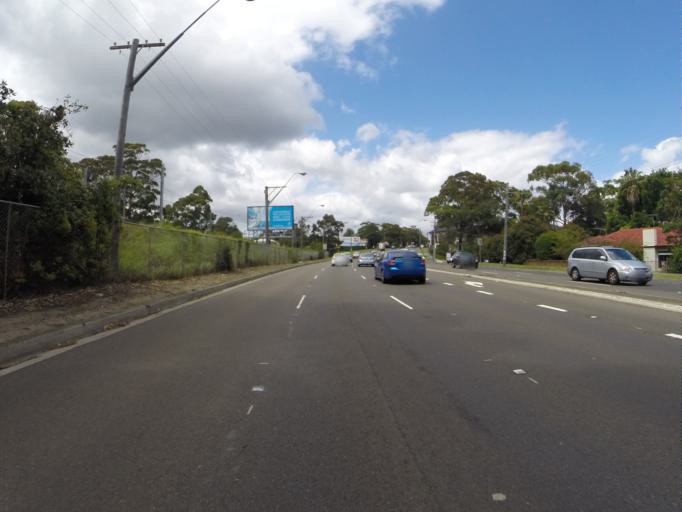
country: AU
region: New South Wales
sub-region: Sutherland Shire
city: Heathcote
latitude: -34.0844
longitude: 151.0109
